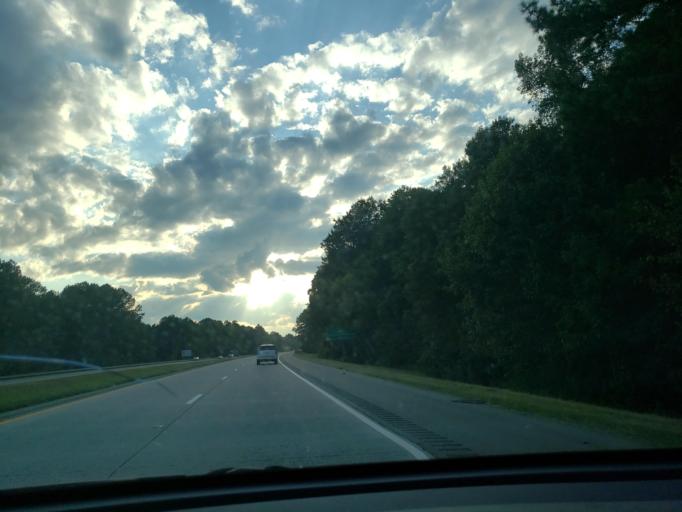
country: US
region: North Carolina
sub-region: Vance County
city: South Henderson
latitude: 36.3195
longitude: -78.4718
